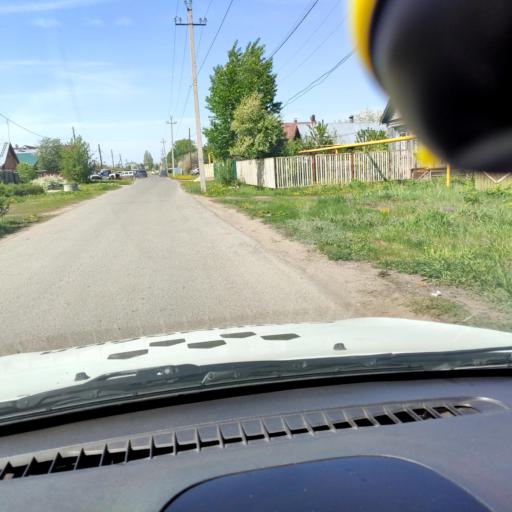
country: RU
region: Samara
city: Tol'yatti
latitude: 53.5725
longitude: 49.3213
